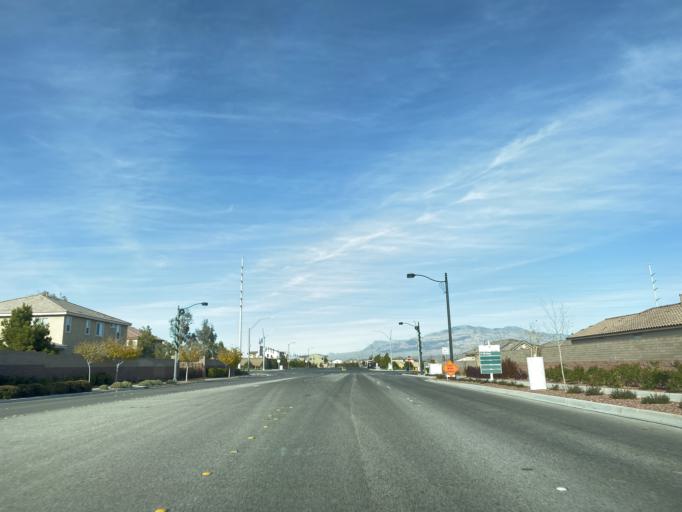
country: US
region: Nevada
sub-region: Clark County
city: Summerlin South
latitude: 36.3054
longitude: -115.3219
